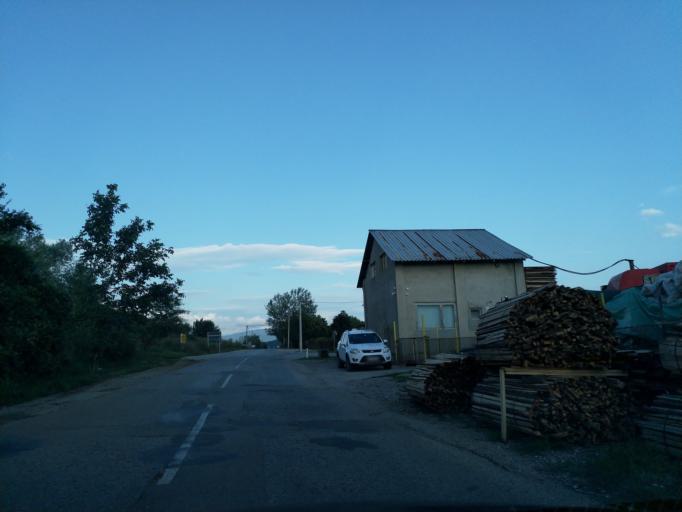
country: RS
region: Central Serbia
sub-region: Rasinski Okrug
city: Cicevac
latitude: 43.7494
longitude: 21.4467
